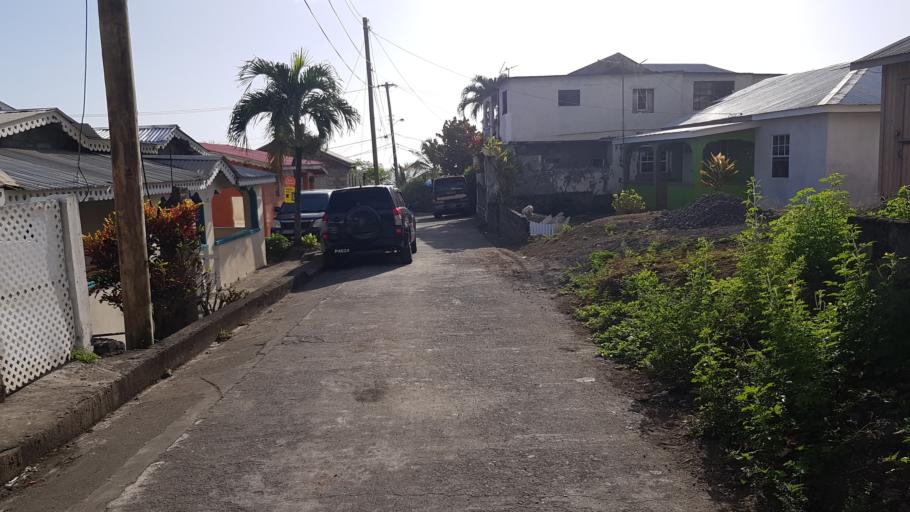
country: VC
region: Charlotte
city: Georgetown
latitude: 13.3502
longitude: -61.1305
